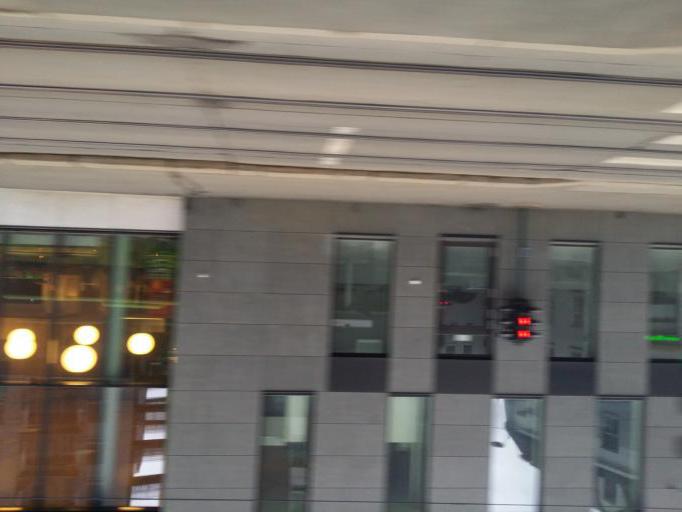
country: NO
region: Oslo
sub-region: Oslo
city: Oslo
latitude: 59.9099
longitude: 10.7638
